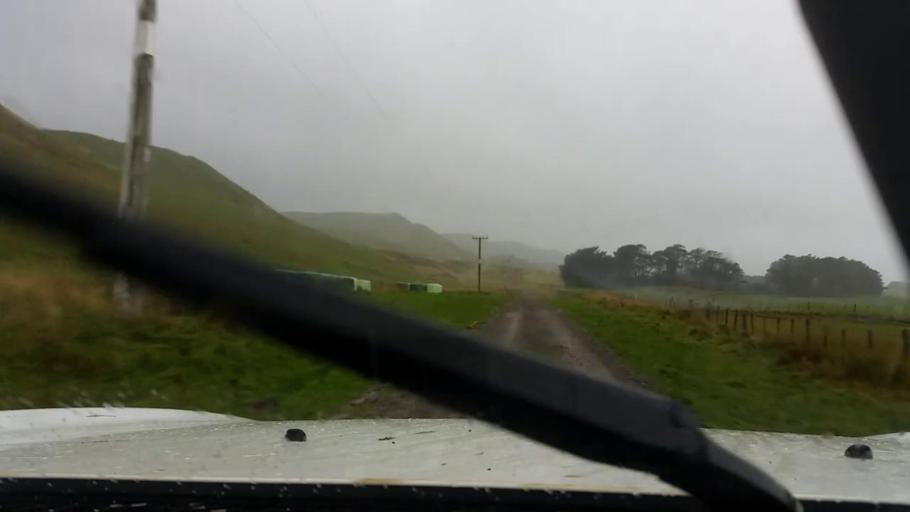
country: NZ
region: Wellington
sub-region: Masterton District
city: Masterton
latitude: -41.2550
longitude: 175.9086
